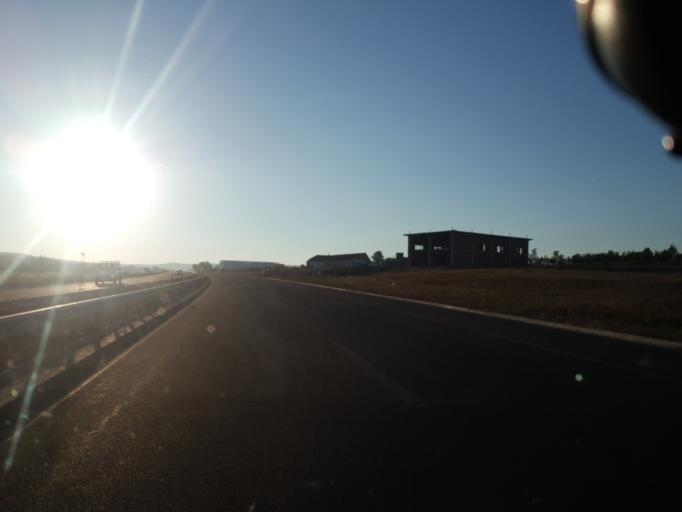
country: XK
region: Prizren
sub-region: Komuna e Malisheves
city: Llazice
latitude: 42.5691
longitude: 20.7376
